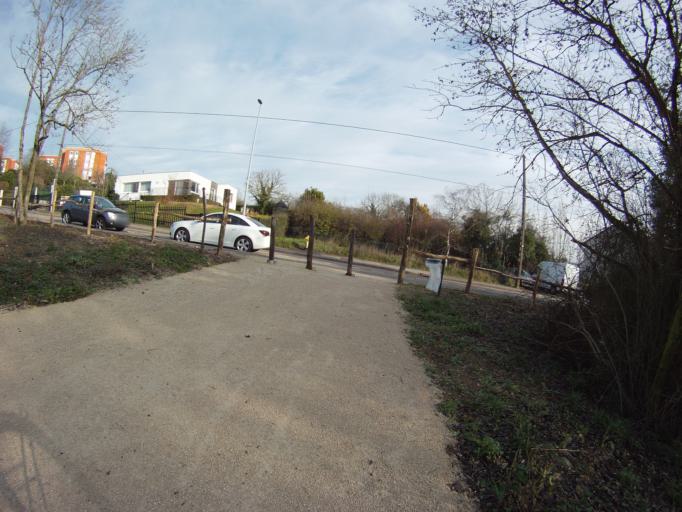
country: FR
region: Lorraine
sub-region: Departement de Meurthe-et-Moselle
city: Saint-Max
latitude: 48.7087
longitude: 6.2056
